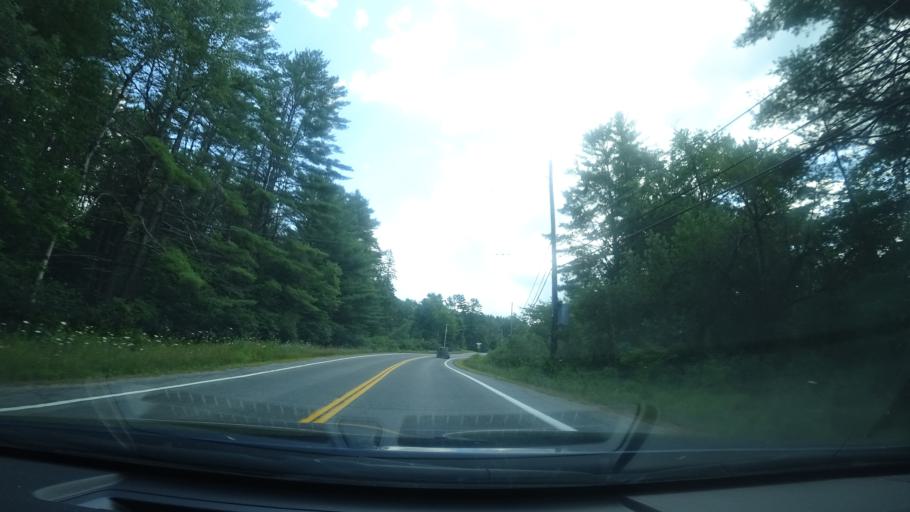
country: US
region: New York
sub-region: Warren County
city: Warrensburg
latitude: 43.6610
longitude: -73.8198
